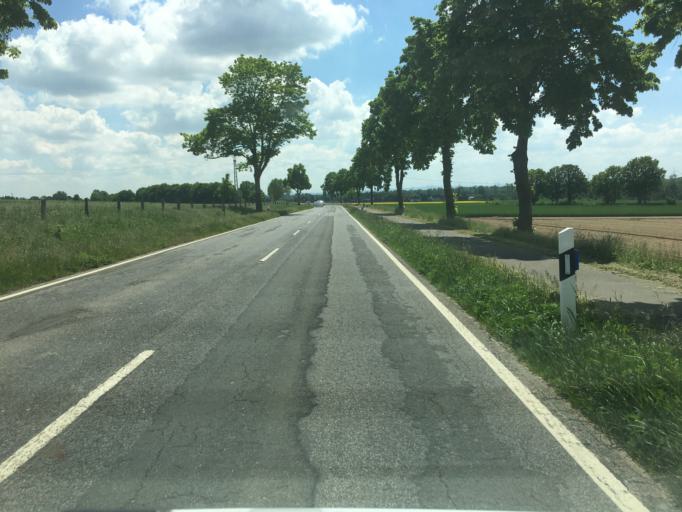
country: DE
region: North Rhine-Westphalia
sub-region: Regierungsbezirk Koln
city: Linnich
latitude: 50.9746
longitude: 6.3119
